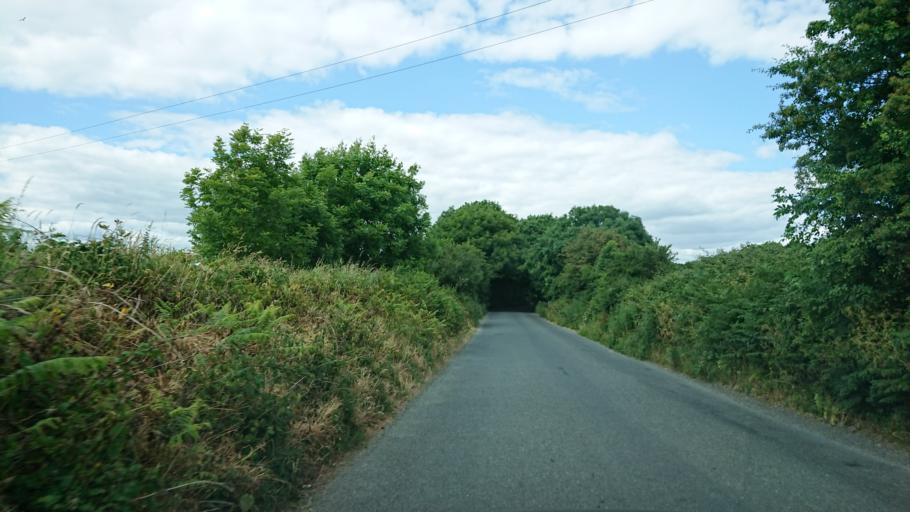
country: IE
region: Munster
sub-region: Waterford
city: Waterford
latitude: 52.2266
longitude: -7.1485
